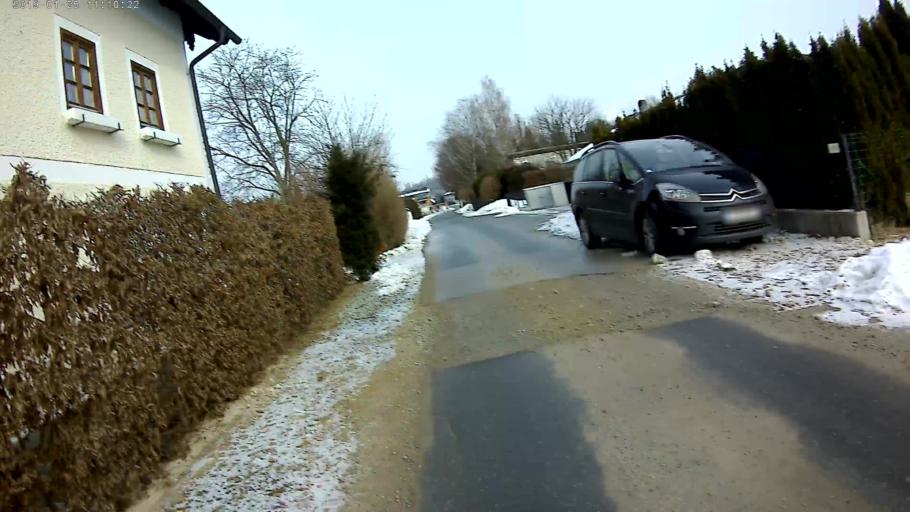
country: AT
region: Salzburg
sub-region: Politischer Bezirk Salzburg-Umgebung
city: Anif
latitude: 47.7449
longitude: 13.0623
